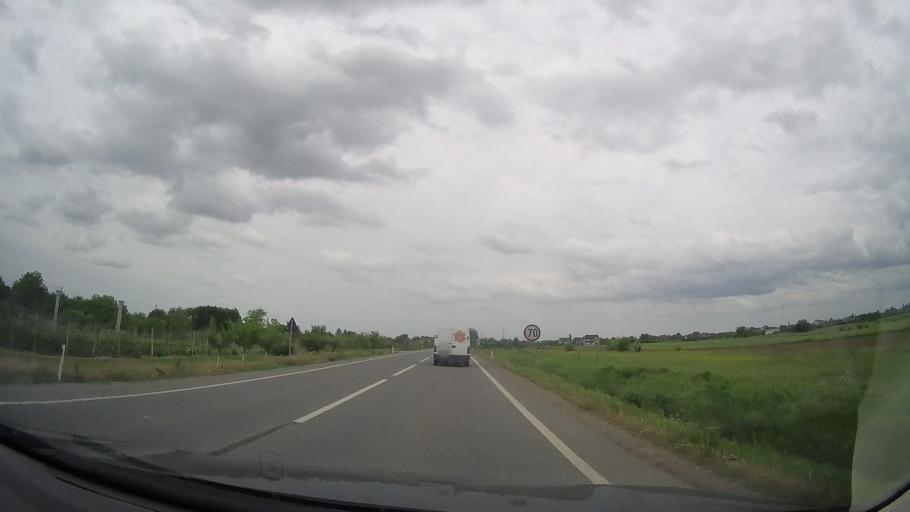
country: RO
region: Dolj
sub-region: Comuna Cosoveni
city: Cosoveni
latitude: 44.2360
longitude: 23.9317
